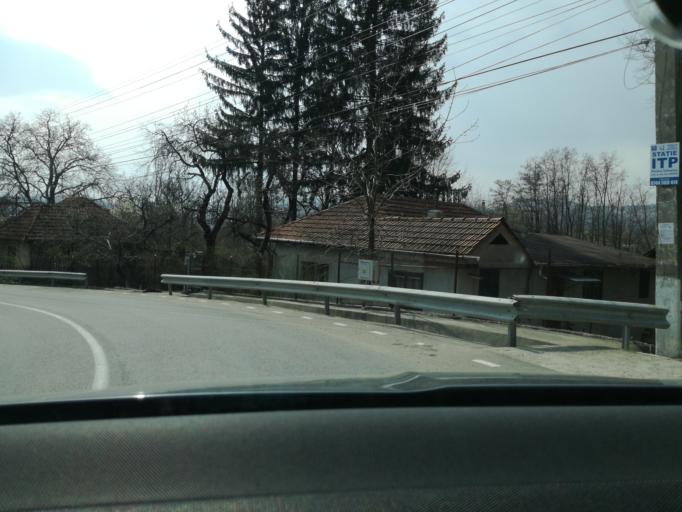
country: RO
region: Prahova
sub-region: Comuna Cornu
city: Cornu de Jos
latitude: 45.1451
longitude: 25.7125
